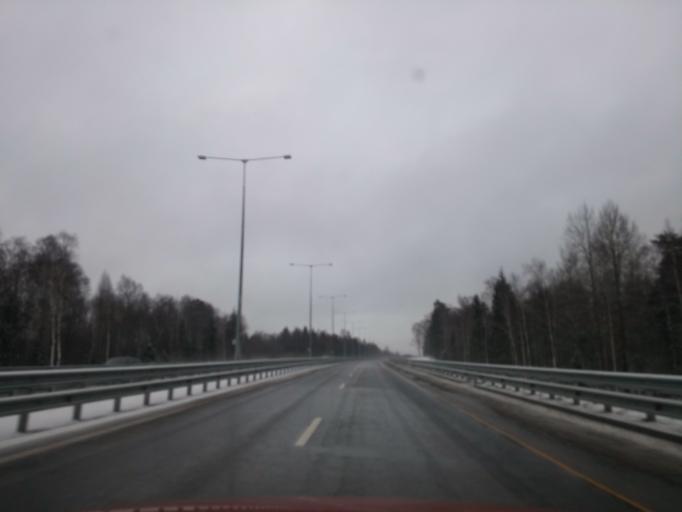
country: RU
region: Tverskaya
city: Likhoslavl'
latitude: 56.9710
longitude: 35.4575
